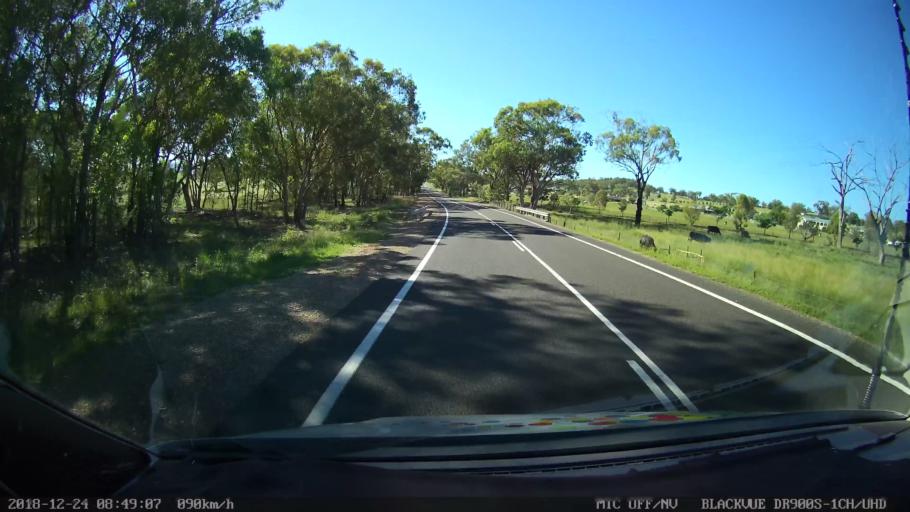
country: AU
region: New South Wales
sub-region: Liverpool Plains
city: Quirindi
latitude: -31.4638
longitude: 150.6509
